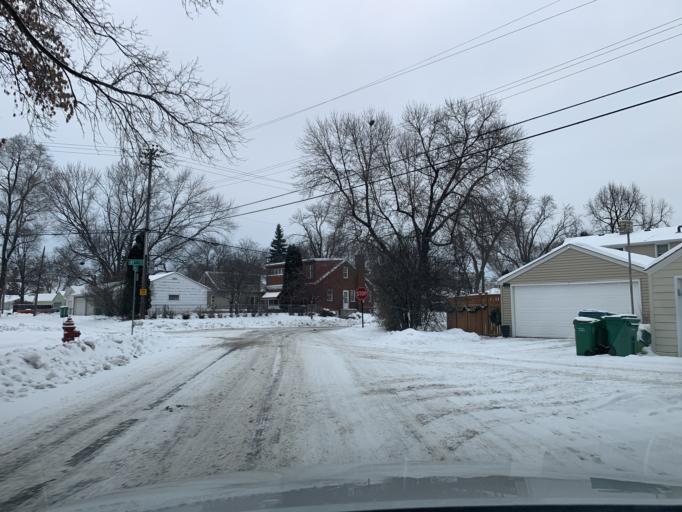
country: US
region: Minnesota
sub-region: Hennepin County
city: Saint Louis Park
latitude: 44.9270
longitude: -93.3457
